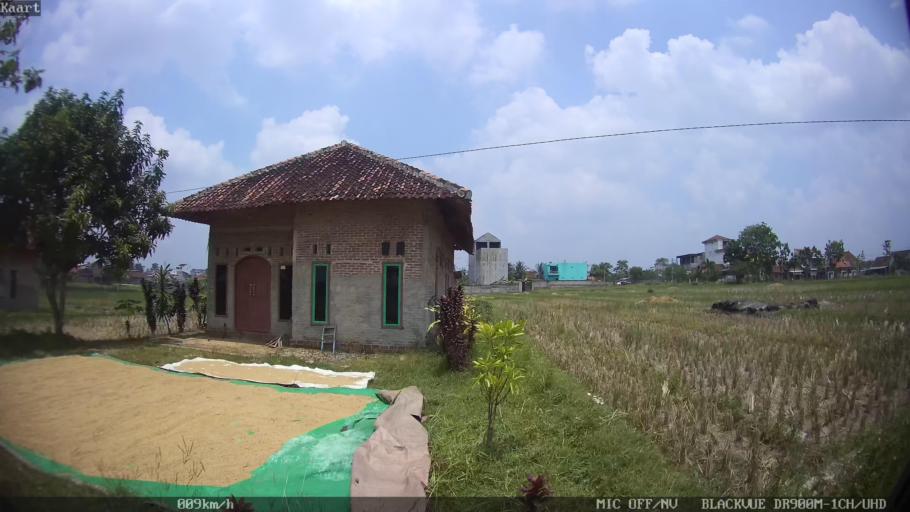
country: ID
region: Lampung
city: Pringsewu
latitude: -5.3545
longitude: 104.9889
